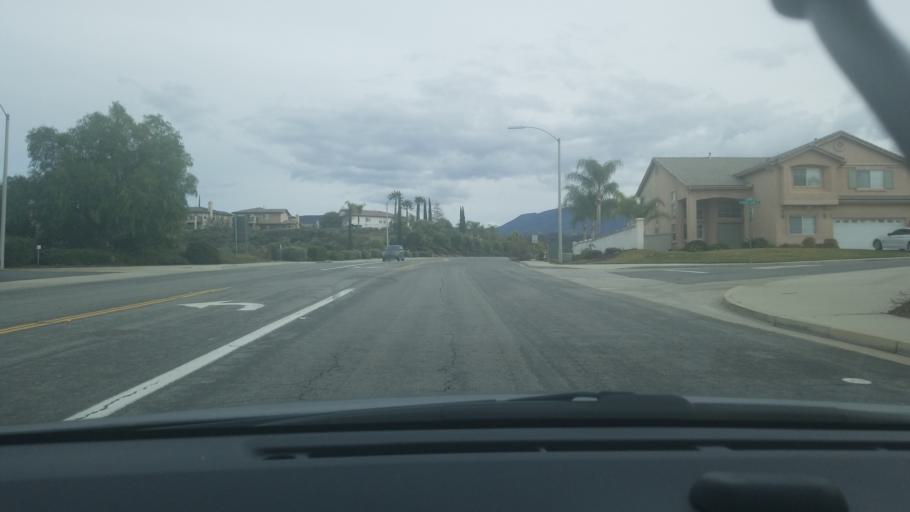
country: US
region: California
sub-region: Riverside County
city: Temecula
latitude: 33.4696
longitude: -117.0747
